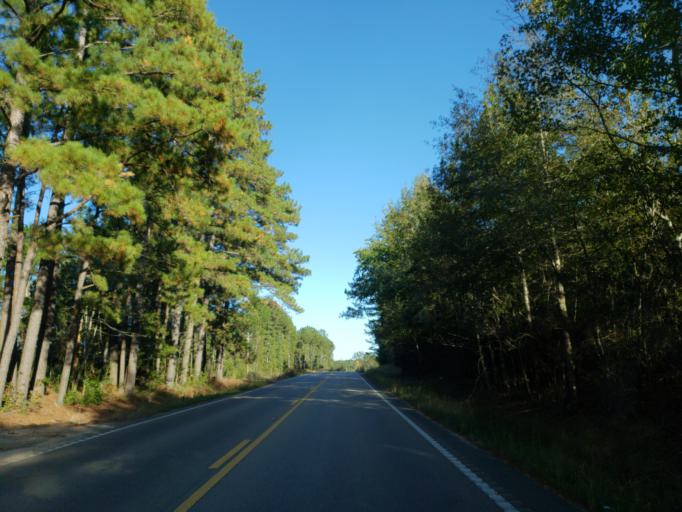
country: US
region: Mississippi
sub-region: Perry County
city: Richton
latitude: 31.3760
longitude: -88.8535
